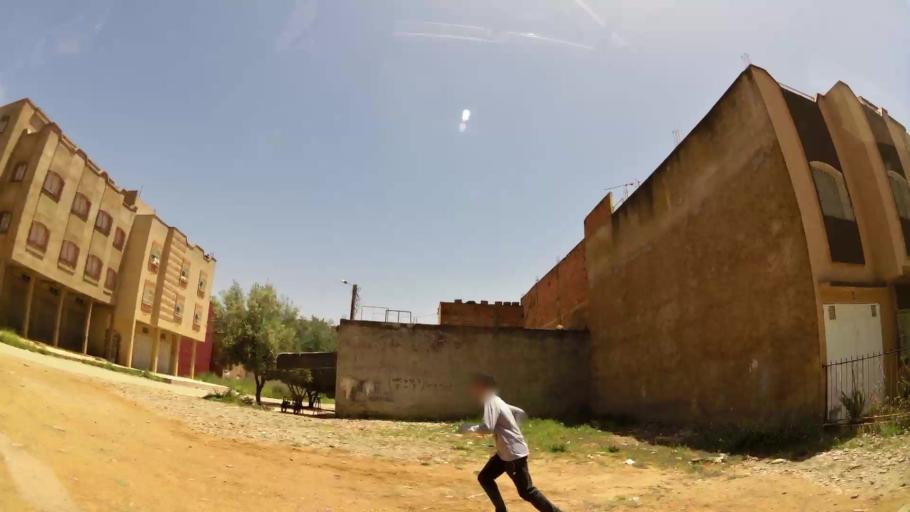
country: MA
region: Rabat-Sale-Zemmour-Zaer
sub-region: Khemisset
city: Khemisset
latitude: 33.8301
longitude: -6.0851
